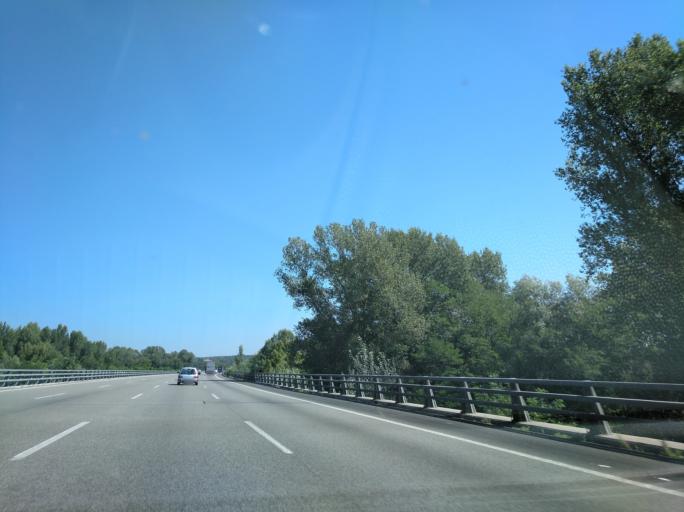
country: ES
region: Catalonia
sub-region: Provincia de Girona
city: Salt
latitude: 41.9814
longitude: 2.7810
